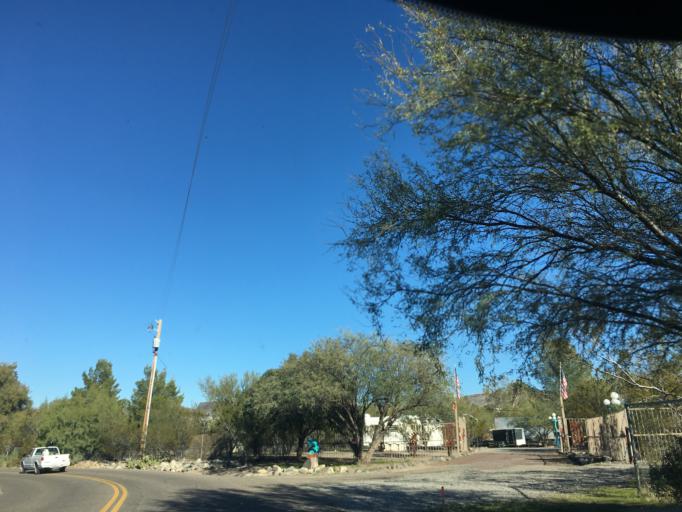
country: US
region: Arizona
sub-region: Yavapai County
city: Black Canyon City
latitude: 34.0642
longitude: -112.1401
